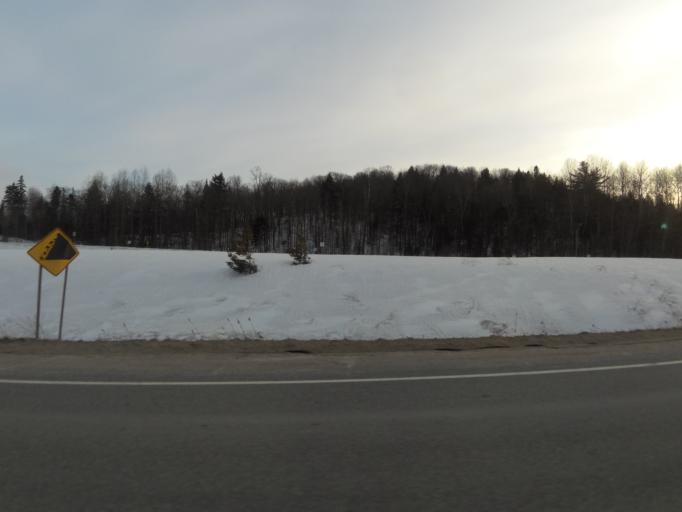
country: CA
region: Quebec
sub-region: Outaouais
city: Wakefield
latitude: 45.6529
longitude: -75.9325
